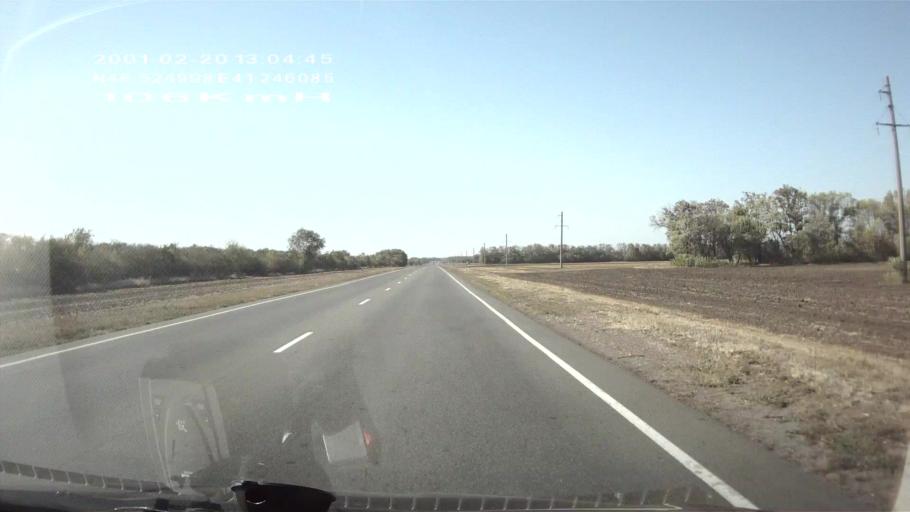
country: RU
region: Rostov
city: Gigant
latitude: 46.5256
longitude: 41.2439
